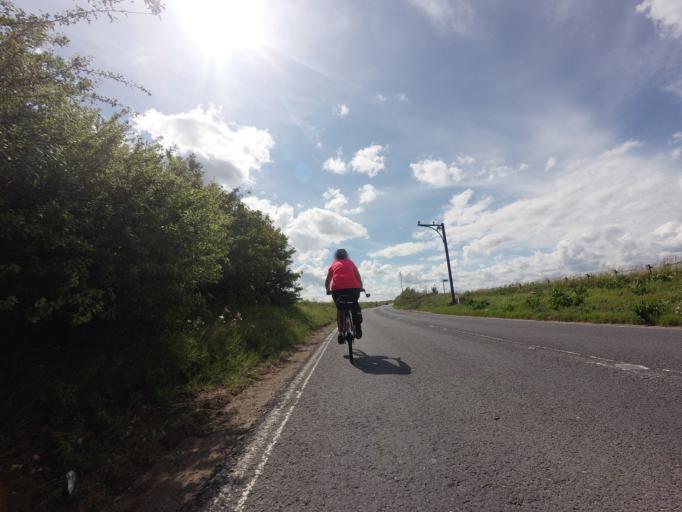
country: GB
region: England
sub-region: Medway
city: Stoke
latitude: 51.4489
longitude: 0.6296
